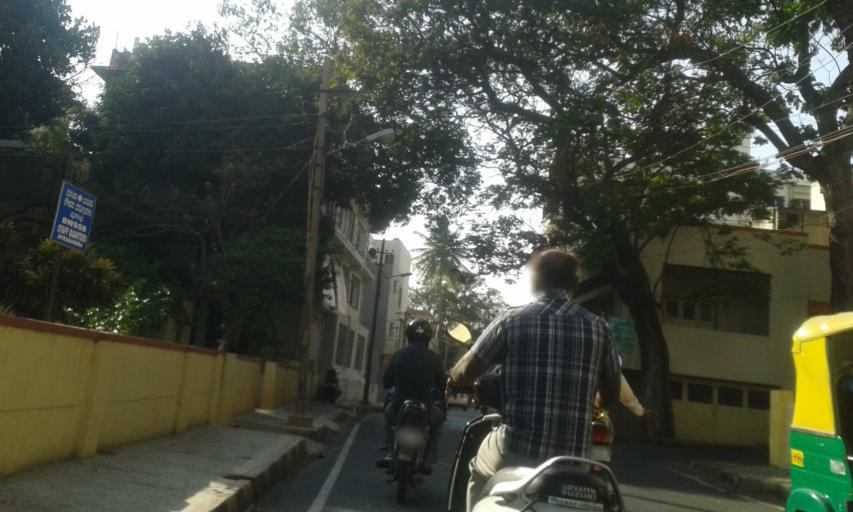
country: IN
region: Karnataka
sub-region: Bangalore Urban
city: Bangalore
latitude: 12.9346
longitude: 77.5880
